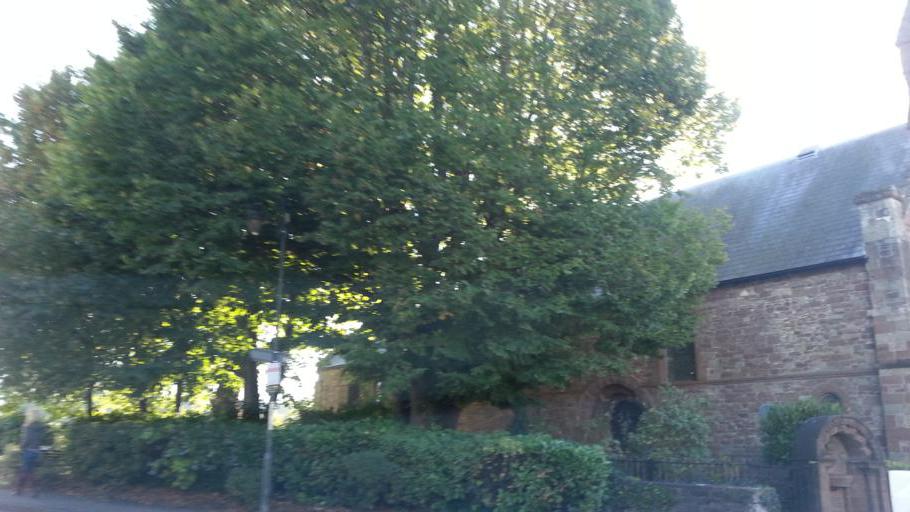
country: GB
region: Wales
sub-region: Monmouthshire
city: Monmouth
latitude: 51.8086
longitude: -2.7207
